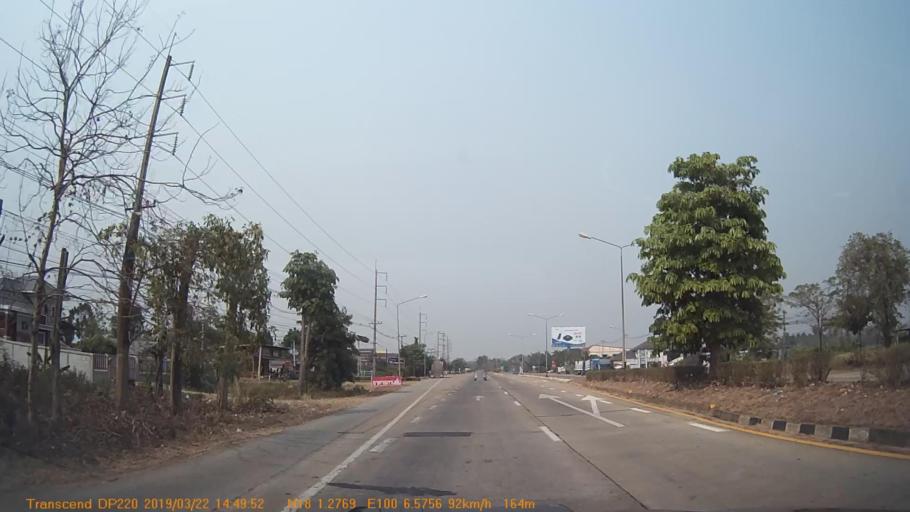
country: TH
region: Phrae
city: Sung Men
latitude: 18.0215
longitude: 100.1097
